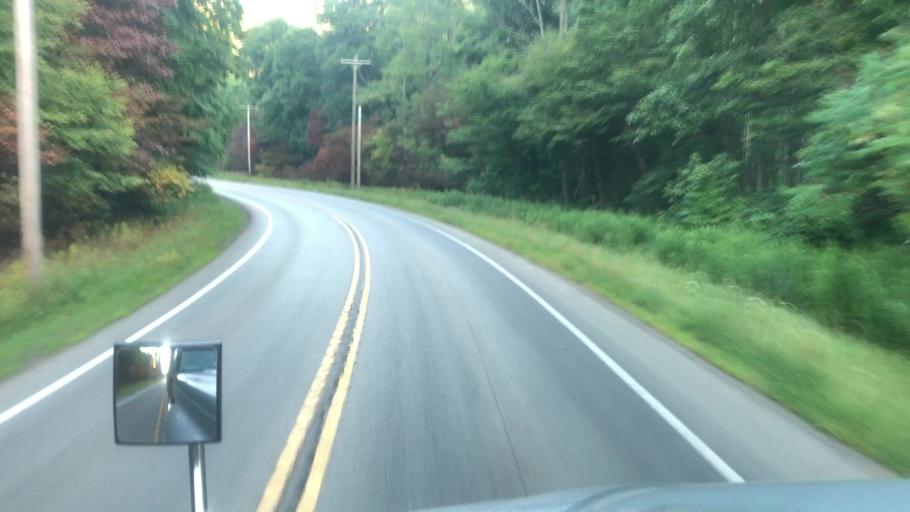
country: US
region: Pennsylvania
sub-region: Venango County
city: Hasson Heights
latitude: 41.4828
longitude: -79.6715
